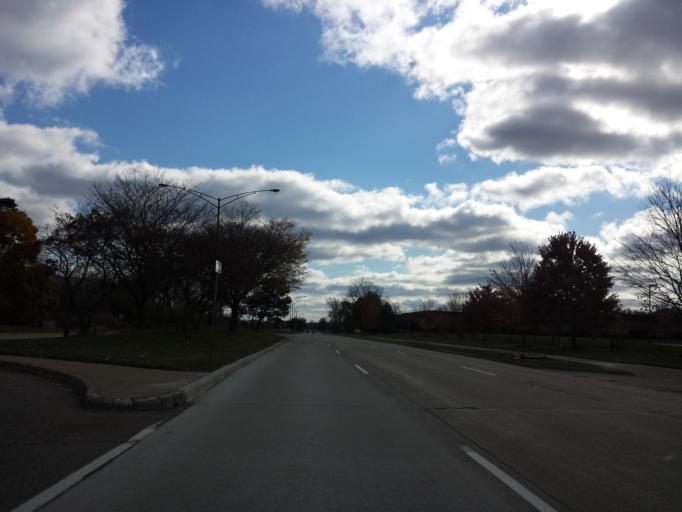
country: US
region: Michigan
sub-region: Oakland County
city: Troy
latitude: 42.5962
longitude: -83.1690
